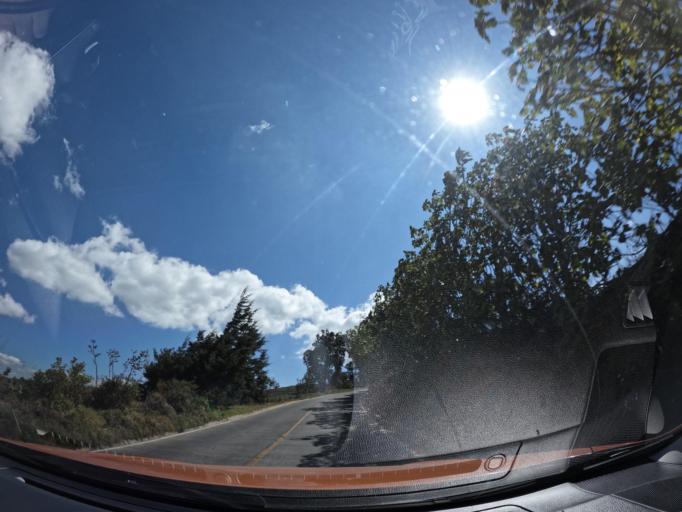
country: GT
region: Chimaltenango
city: Patzun
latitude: 14.6605
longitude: -91.0544
